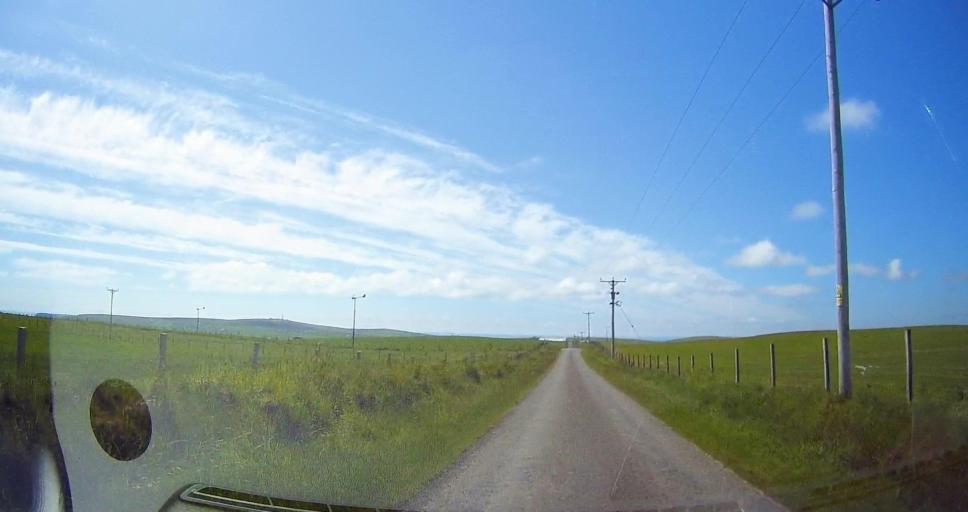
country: GB
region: Scotland
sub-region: Orkney Islands
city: Kirkwall
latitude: 58.8121
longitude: -2.9255
